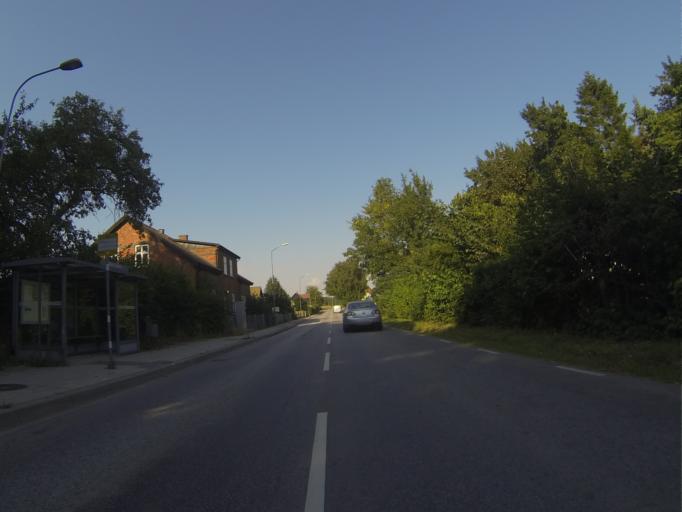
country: SE
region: Skane
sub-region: Svedala Kommun
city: Klagerup
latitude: 55.5796
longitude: 13.1943
